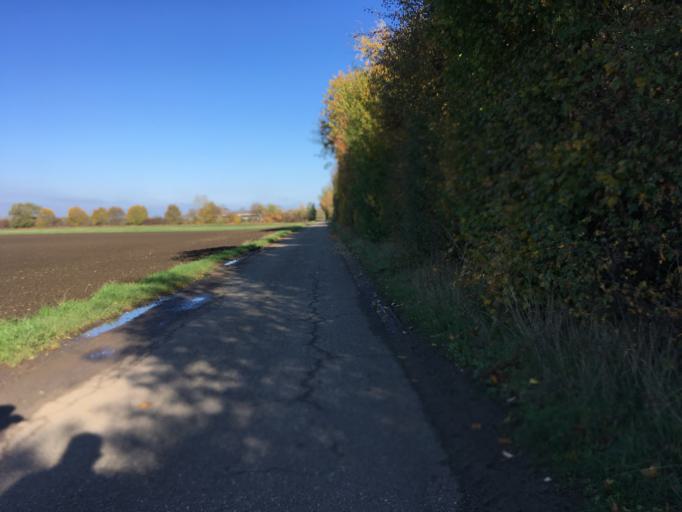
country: DE
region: Hesse
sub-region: Regierungsbezirk Darmstadt
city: Burstadt
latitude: 49.6507
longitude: 8.4708
